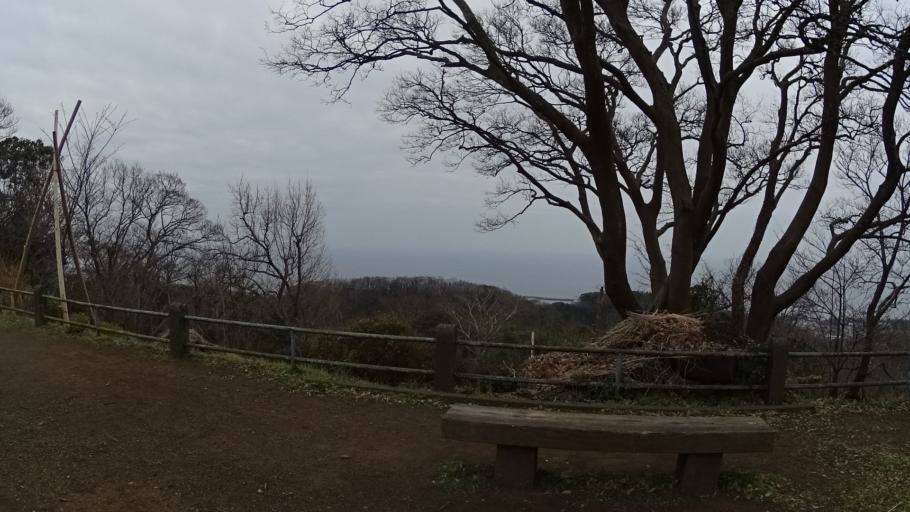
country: JP
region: Kanagawa
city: Oiso
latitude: 35.3198
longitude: 139.3091
